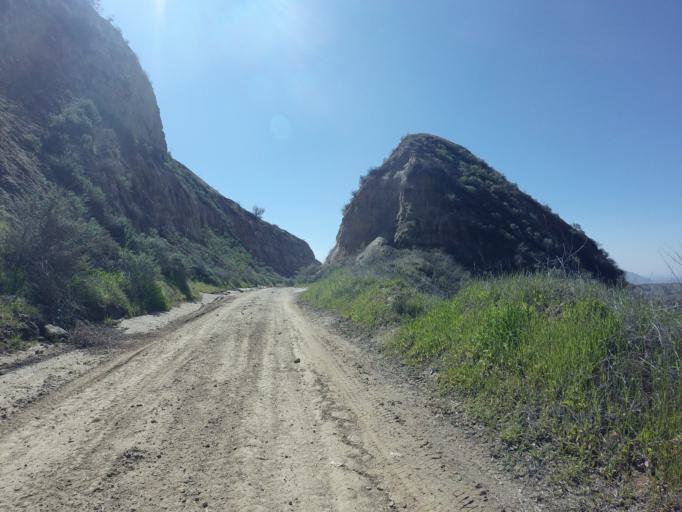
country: US
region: California
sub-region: Riverside County
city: Beaumont
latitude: 33.9281
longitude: -117.0387
